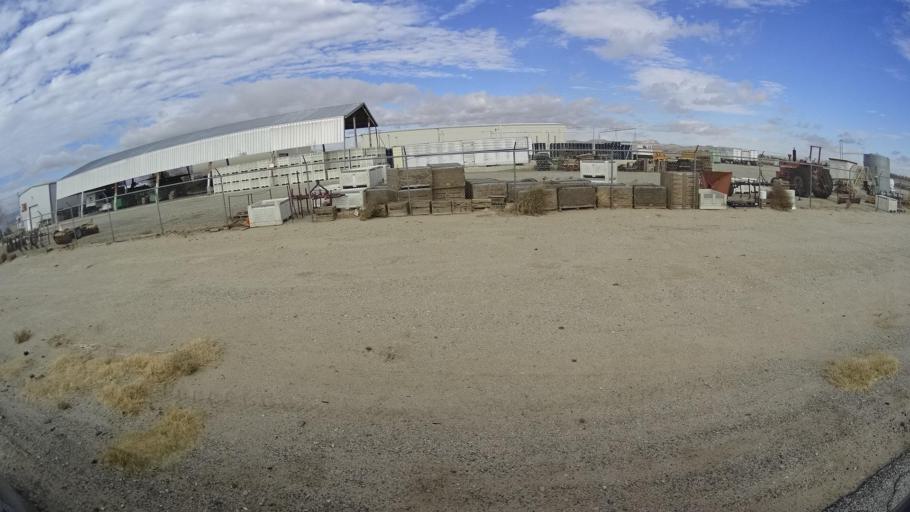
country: US
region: California
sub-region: Kern County
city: Rosamond
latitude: 34.8201
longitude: -118.2794
